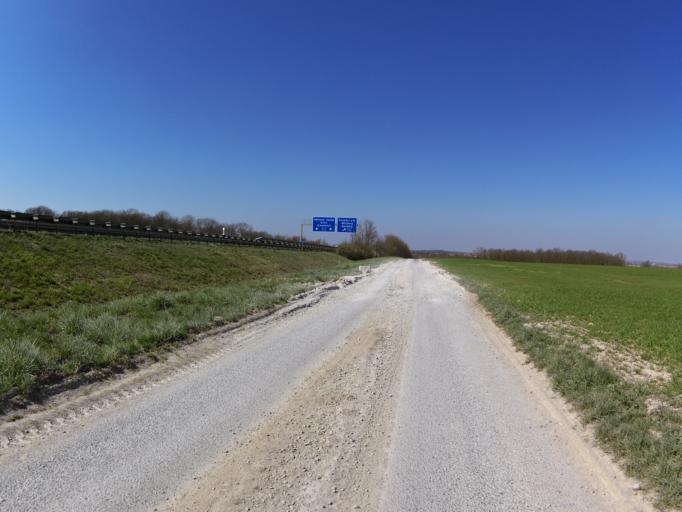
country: DE
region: Bavaria
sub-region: Regierungsbezirk Unterfranken
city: Biebelried
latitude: 49.7718
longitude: 10.0985
